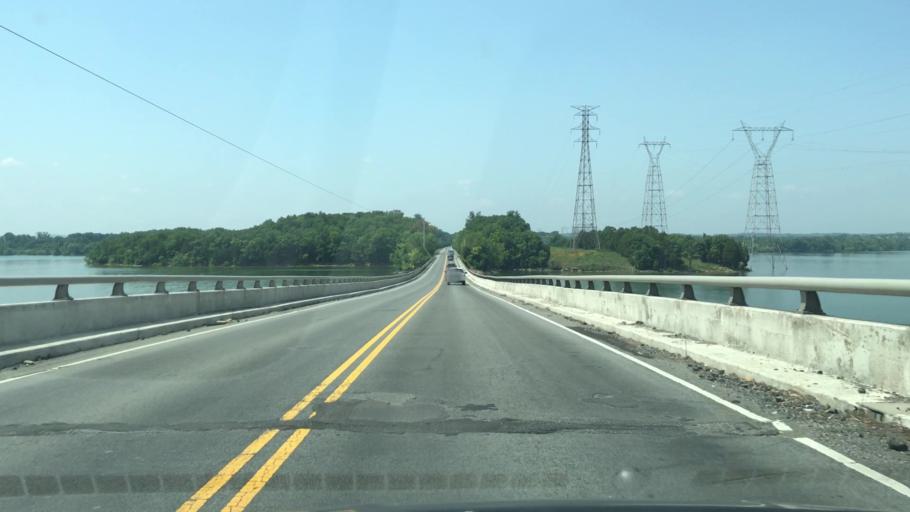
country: US
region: Tennessee
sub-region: Rutherford County
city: La Vergne
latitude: 36.0847
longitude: -86.5650
